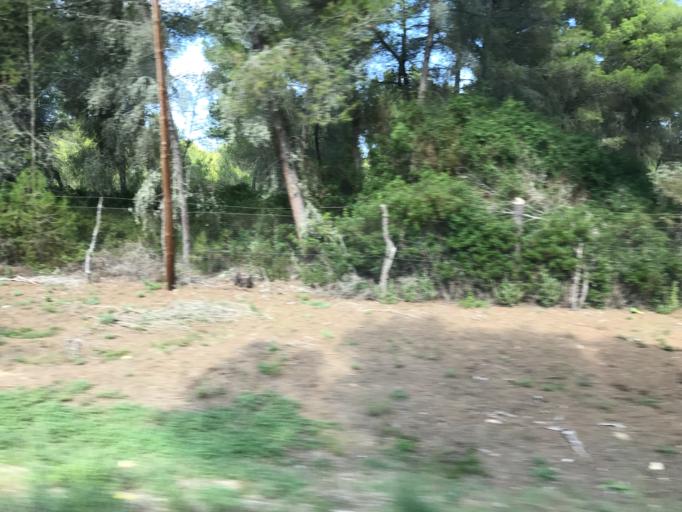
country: ES
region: Balearic Islands
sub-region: Illes Balears
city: Santa Margalida
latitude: 39.7311
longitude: 3.1904
